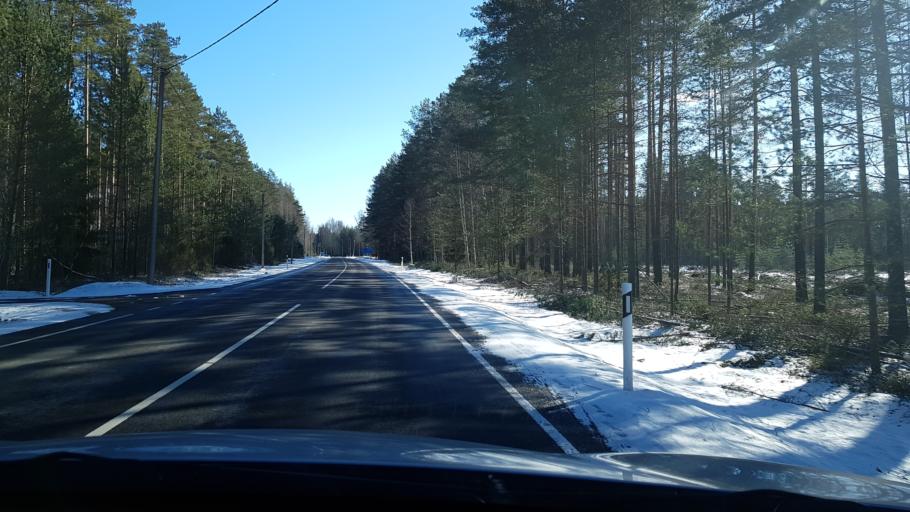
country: EE
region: Polvamaa
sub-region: Raepina vald
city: Rapina
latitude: 57.9804
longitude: 27.5689
